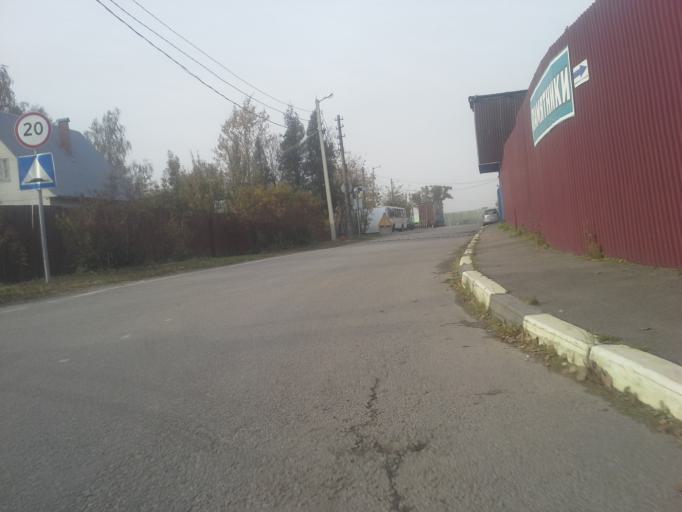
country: RU
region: Moskovskaya
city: Golitsyno
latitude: 55.6003
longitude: 36.9971
